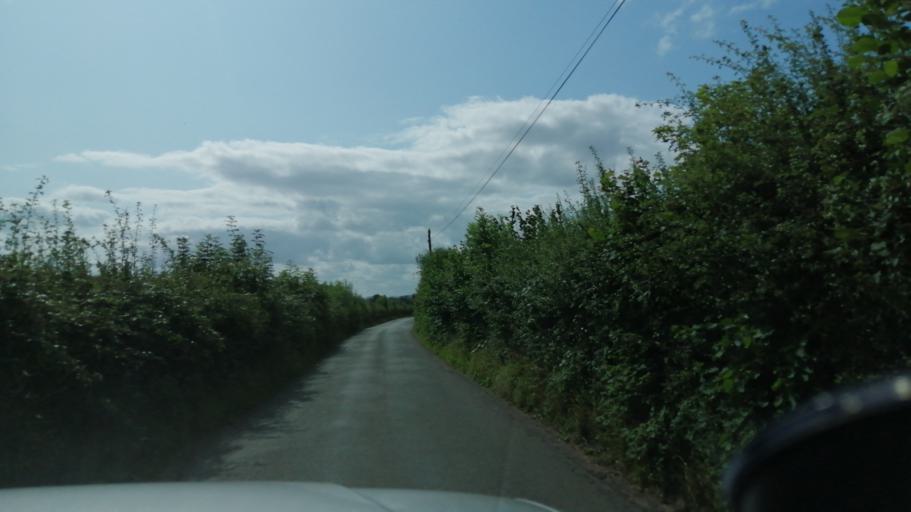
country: GB
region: England
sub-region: Herefordshire
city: Kinnersley
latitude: 52.1317
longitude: -2.9630
